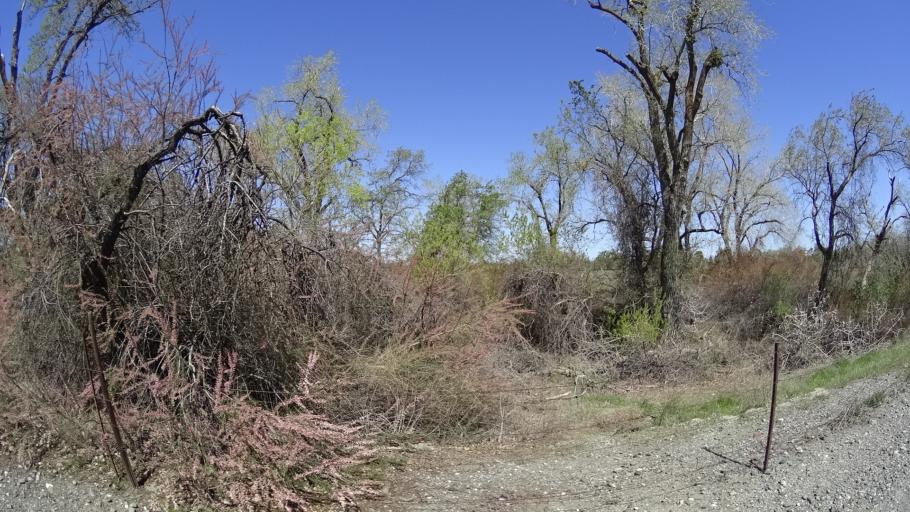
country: US
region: California
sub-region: Glenn County
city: Orland
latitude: 39.7841
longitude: -122.2499
